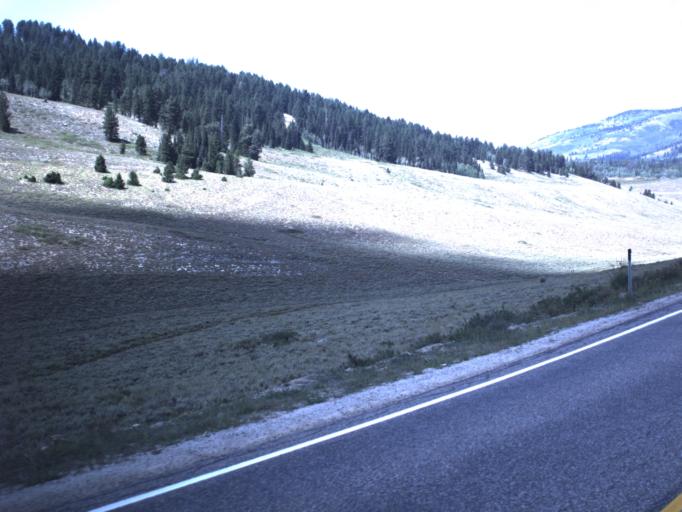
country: US
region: Idaho
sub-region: Bear Lake County
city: Paris
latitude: 41.9371
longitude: -111.4811
